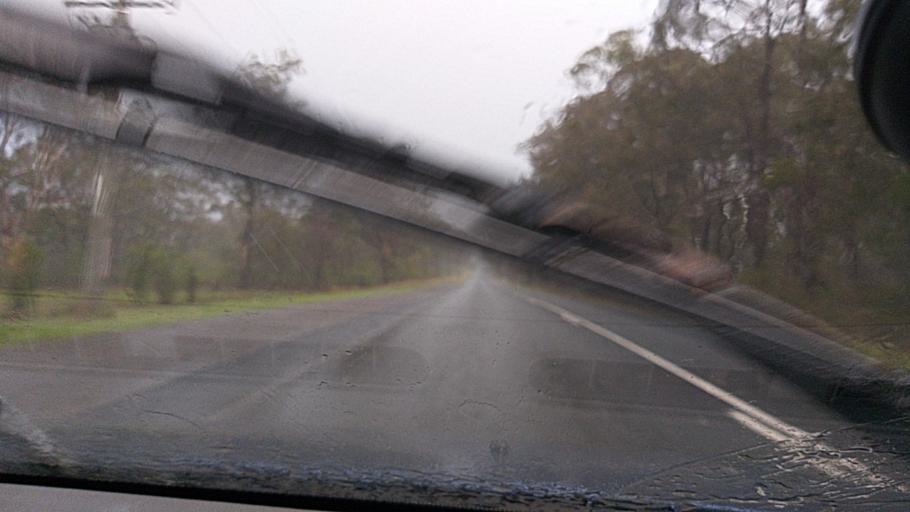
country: AU
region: New South Wales
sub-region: Wollondilly
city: Douglas Park
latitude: -34.2226
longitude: 150.7253
